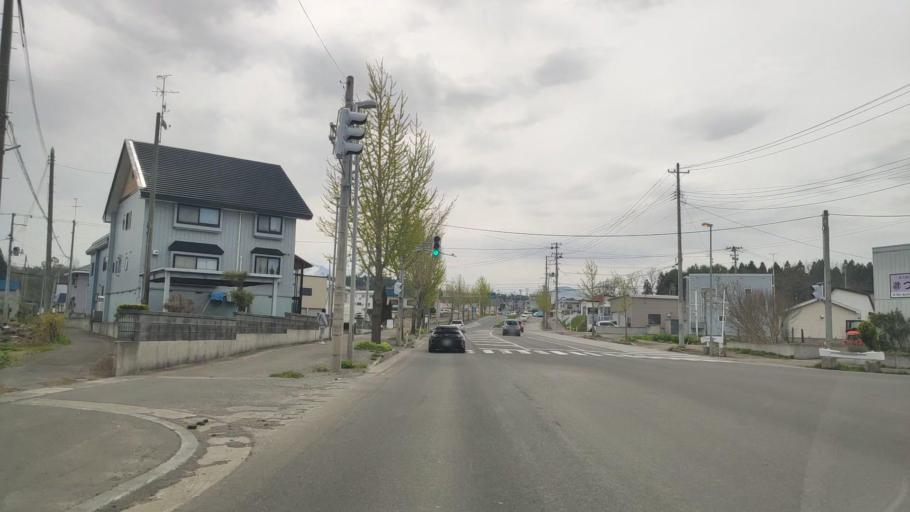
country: JP
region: Aomori
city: Aomori Shi
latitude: 40.7923
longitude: 140.7864
